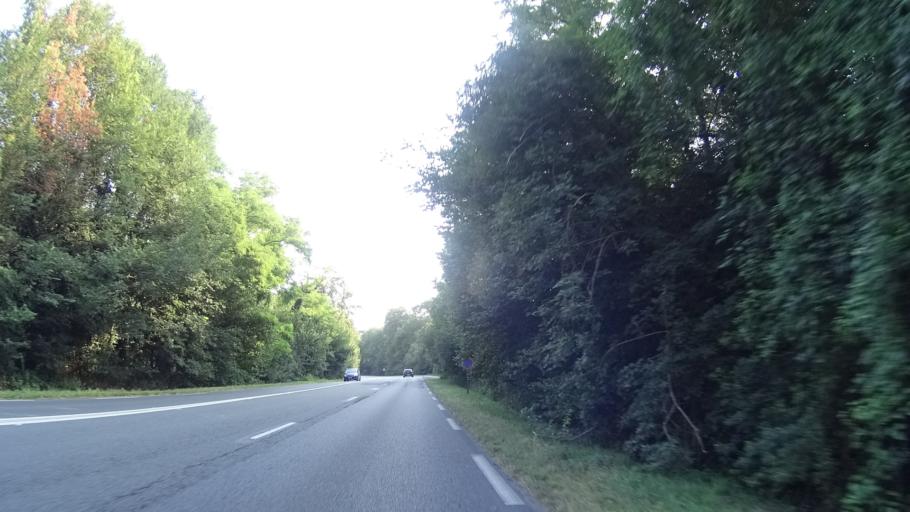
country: FR
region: Ile-de-France
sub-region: Departement du Val-d'Oise
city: Chaumontel
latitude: 49.1332
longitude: 2.4348
